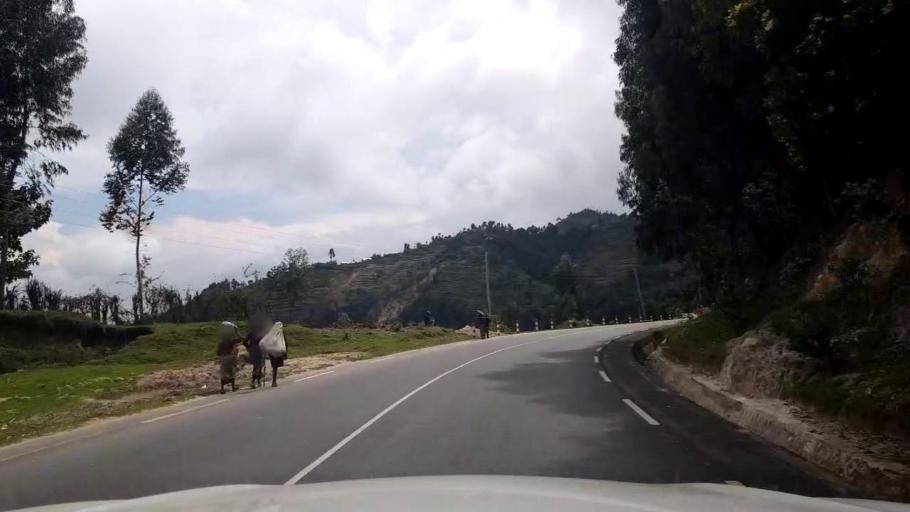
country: RW
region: Northern Province
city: Musanze
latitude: -1.6658
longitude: 29.5176
